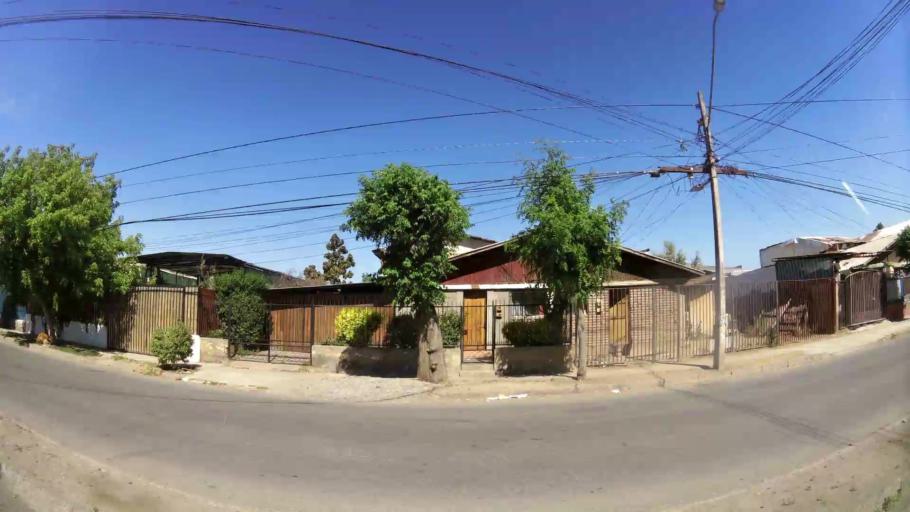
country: CL
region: Santiago Metropolitan
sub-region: Provincia de Maipo
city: San Bernardo
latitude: -33.5808
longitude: -70.6833
